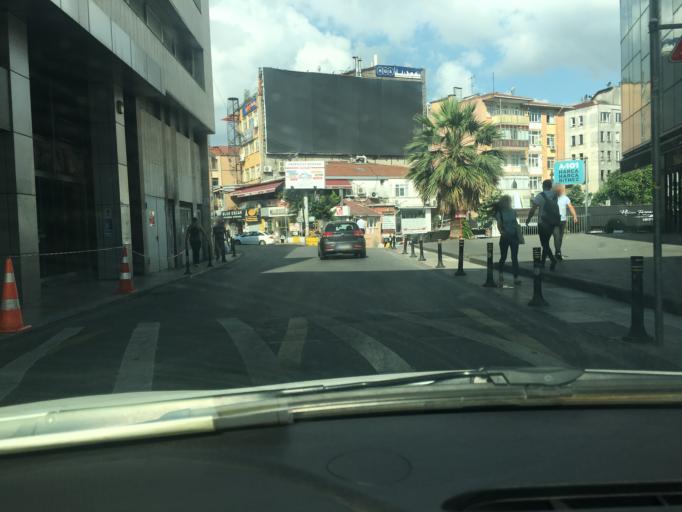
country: TR
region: Istanbul
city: Sisli
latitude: 41.0696
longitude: 29.0012
